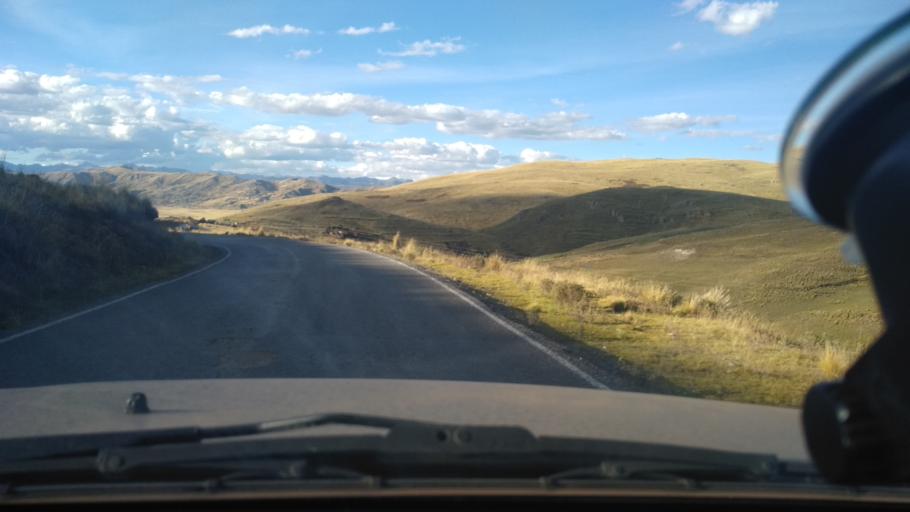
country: PE
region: Cusco
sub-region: Provincia de Canas
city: Ccaquiracunca
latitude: -14.2805
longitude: -71.4491
